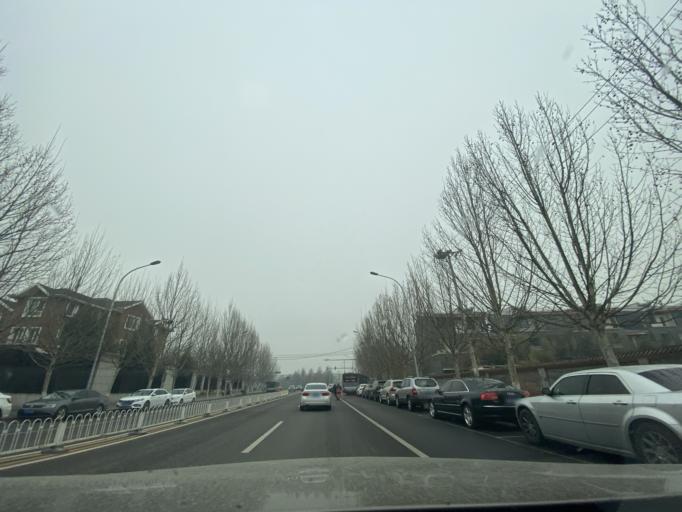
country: CN
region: Beijing
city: Sijiqing
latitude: 39.9707
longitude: 116.2402
